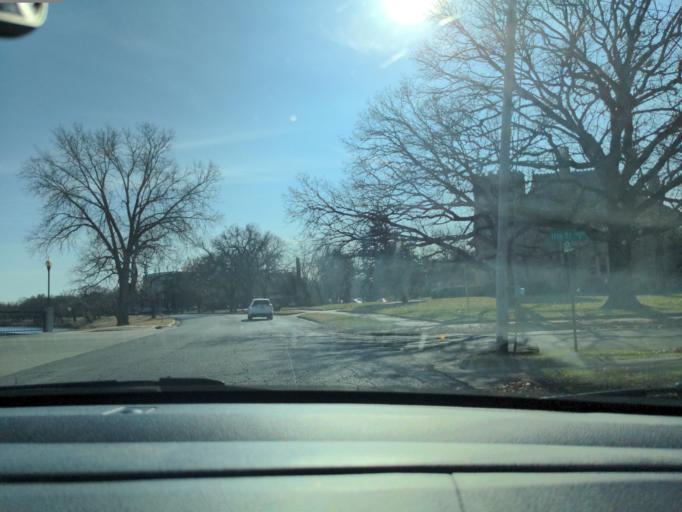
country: US
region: Kansas
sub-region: Sedgwick County
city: Wichita
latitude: 37.7050
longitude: -97.3585
